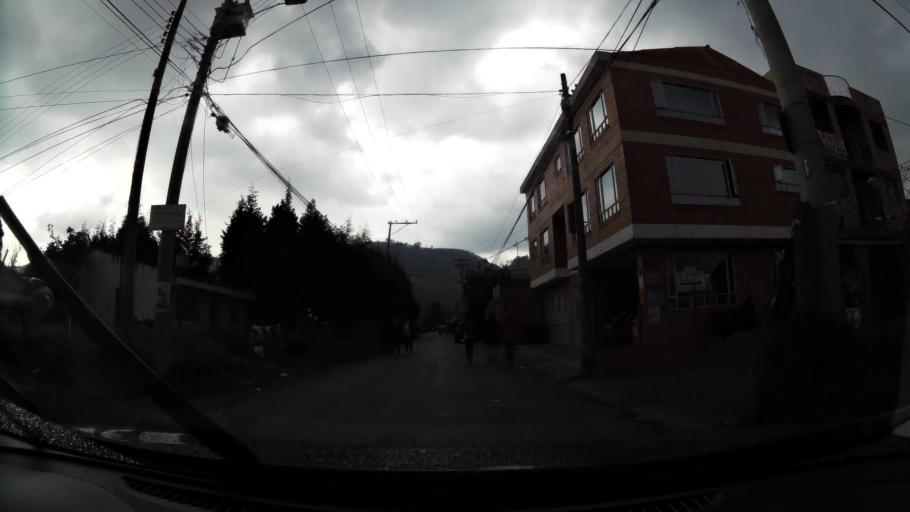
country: CO
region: Cundinamarca
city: Chia
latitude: 4.8564
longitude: -74.0716
